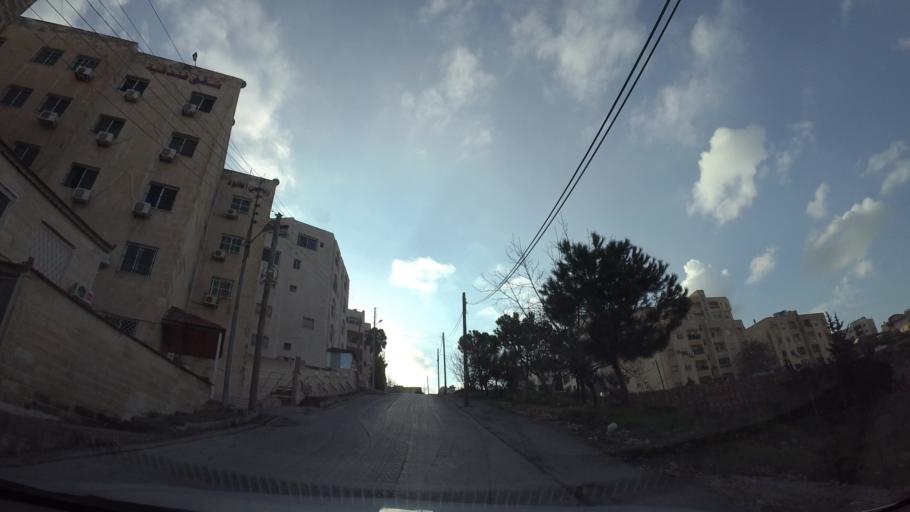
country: JO
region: Amman
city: Al Jubayhah
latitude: 32.0057
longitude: 35.8690
